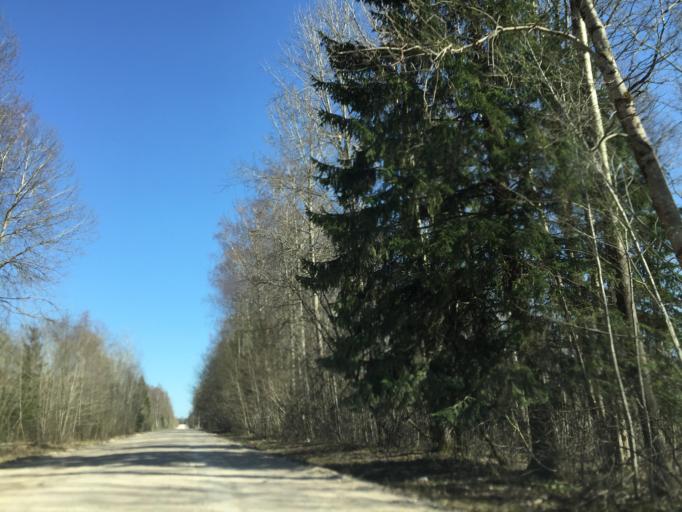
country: LV
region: Malpils
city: Malpils
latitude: 57.0246
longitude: 24.9878
